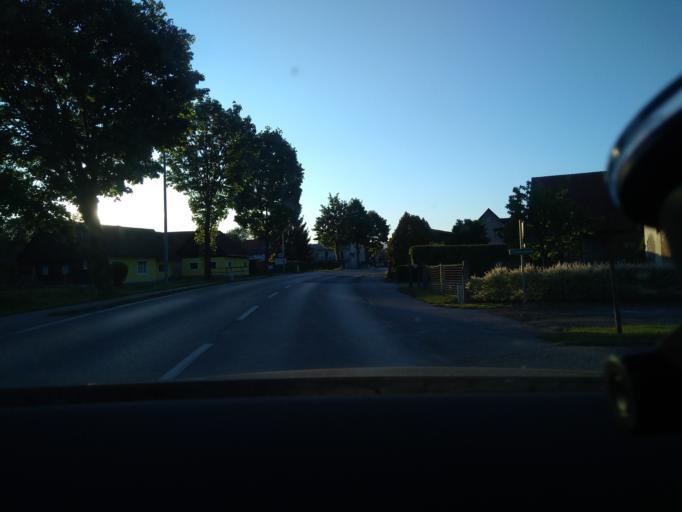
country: AT
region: Styria
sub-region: Politischer Bezirk Voitsberg
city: Mooskirchen
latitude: 46.9985
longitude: 15.2928
